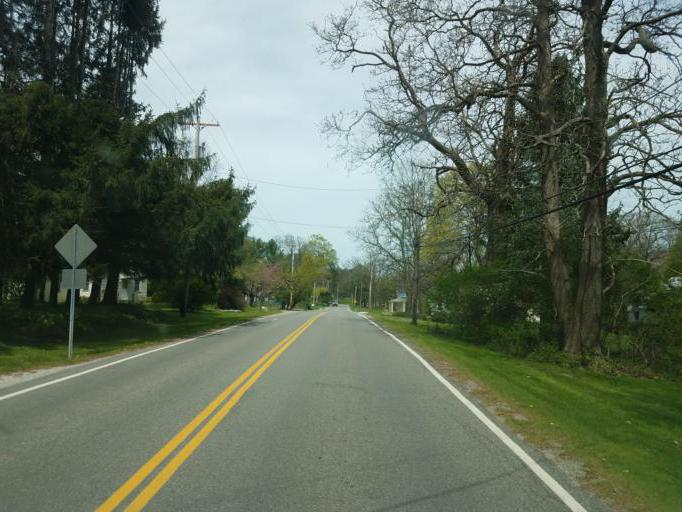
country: US
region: Ohio
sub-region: Summit County
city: Peninsula
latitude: 41.2434
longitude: -81.5563
